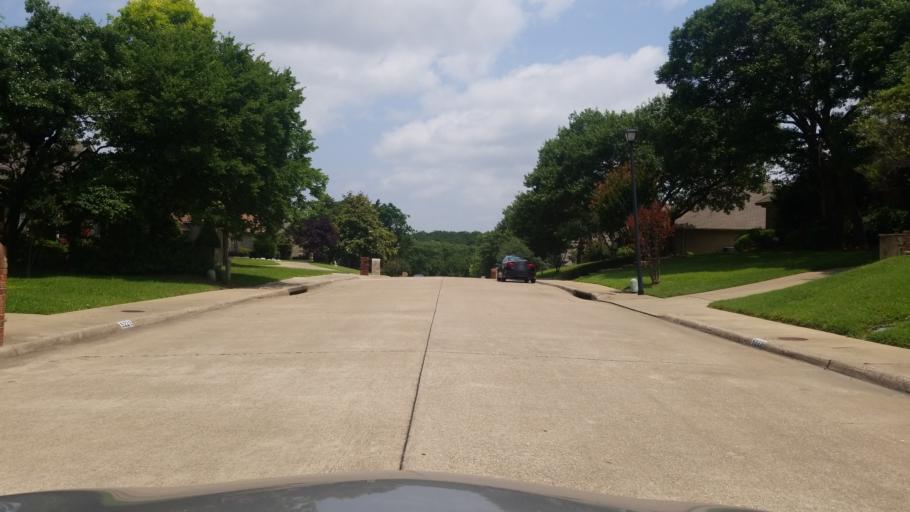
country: US
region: Texas
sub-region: Dallas County
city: Duncanville
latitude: 32.6823
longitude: -96.9234
